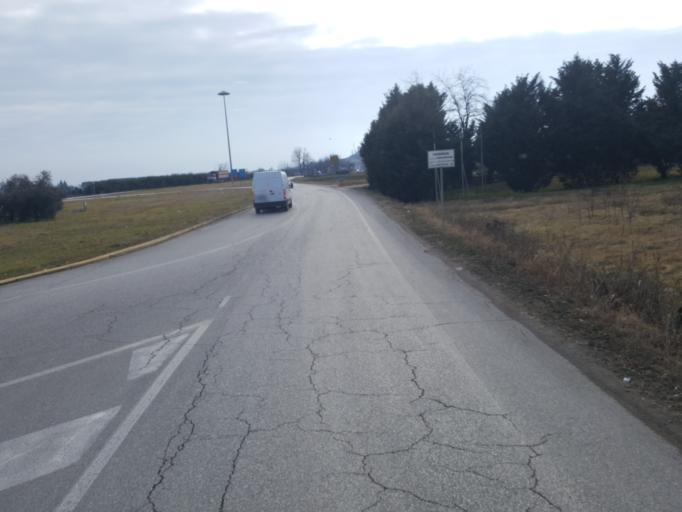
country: IT
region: Veneto
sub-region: Provincia di Verona
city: Sona
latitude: 45.4398
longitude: 10.8507
